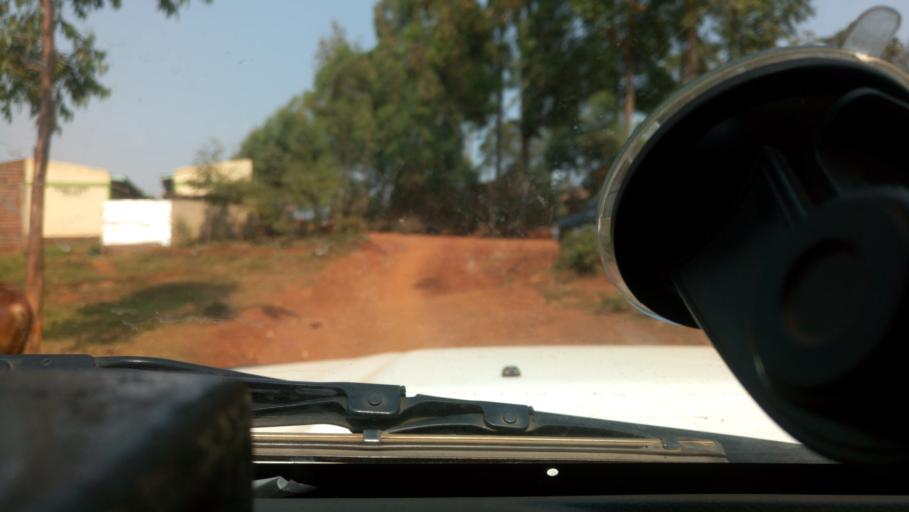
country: KE
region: Kisii
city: Ogembo
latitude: -0.8257
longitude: 34.6164
